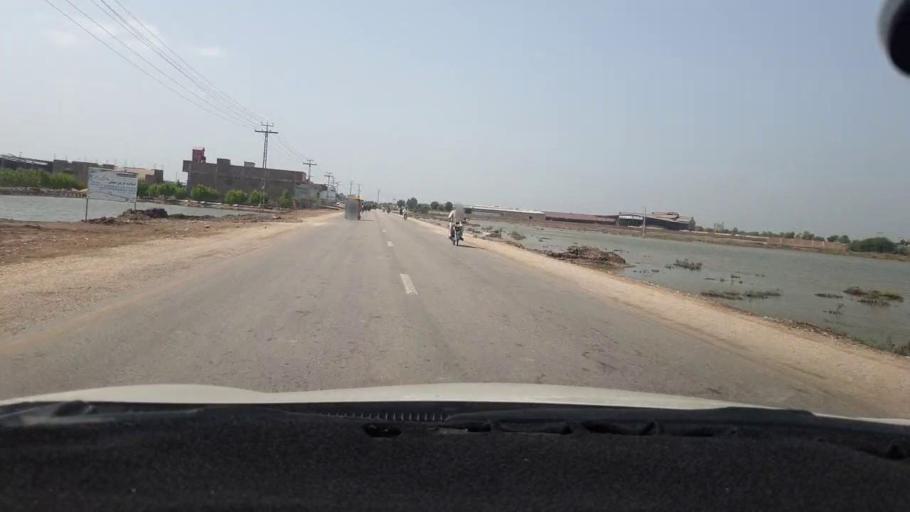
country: PK
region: Sindh
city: Mirpur Khas
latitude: 25.5518
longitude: 69.0490
